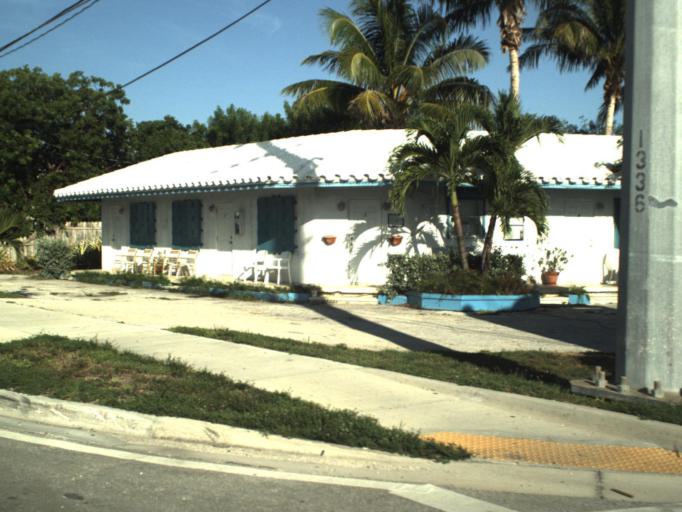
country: US
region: Florida
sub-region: Monroe County
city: Marathon
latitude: 24.7218
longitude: -81.0576
